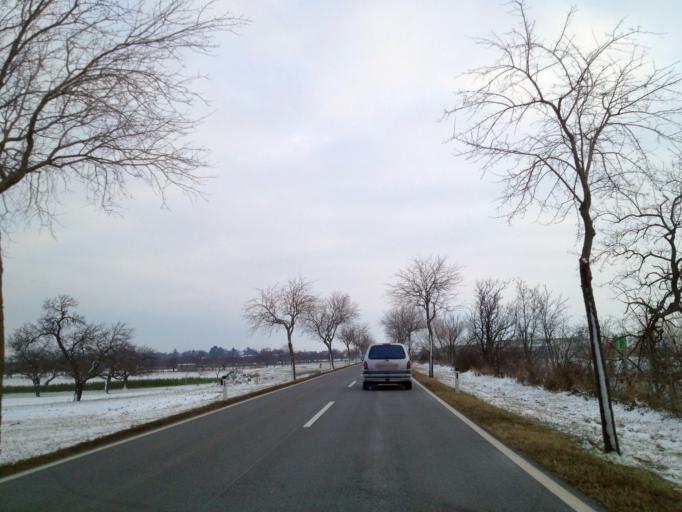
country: AT
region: Lower Austria
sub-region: Politischer Bezirk Bruck an der Leitha
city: Berg
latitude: 48.0996
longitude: 17.0469
